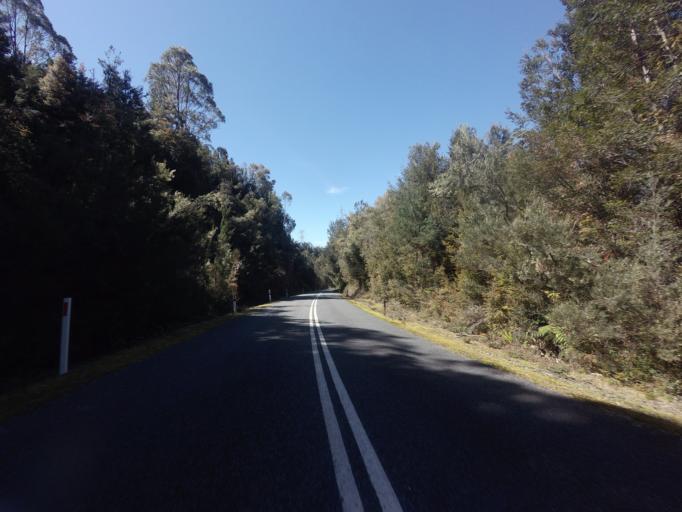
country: AU
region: Tasmania
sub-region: Huon Valley
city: Geeveston
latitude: -42.8149
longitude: 146.3683
